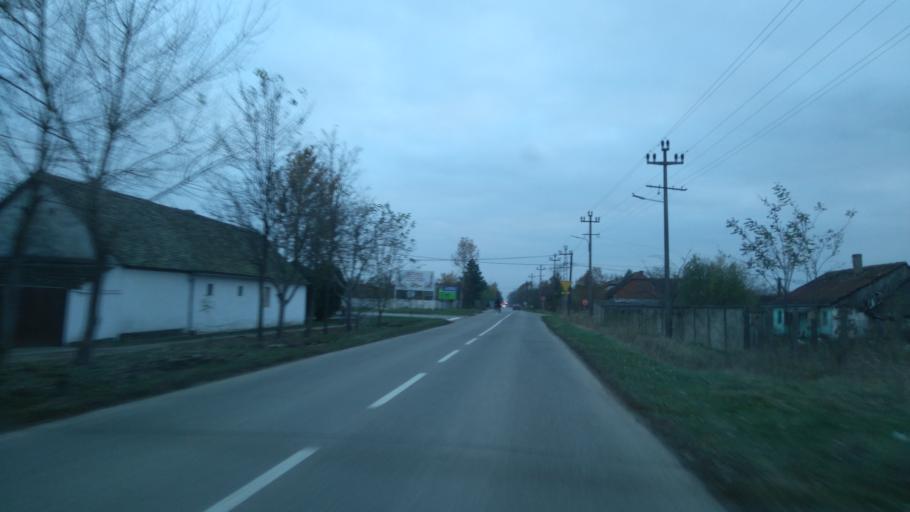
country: RS
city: Mol
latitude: 45.7726
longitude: 20.1285
